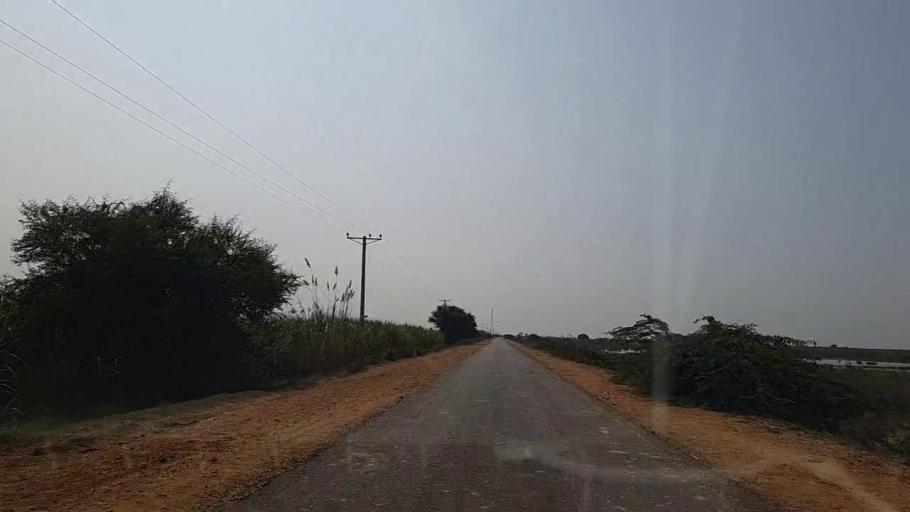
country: PK
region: Sindh
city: Chuhar Jamali
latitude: 24.2952
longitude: 67.9292
